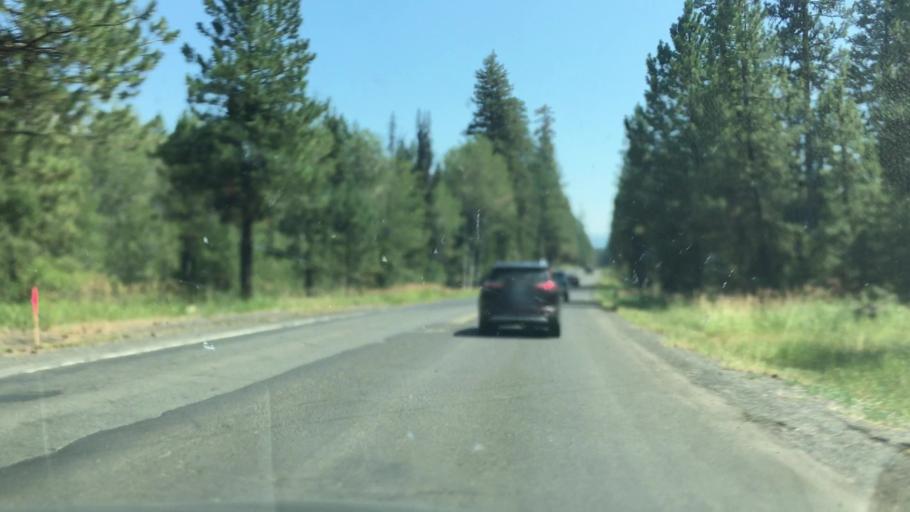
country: US
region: Idaho
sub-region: Valley County
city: McCall
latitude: 44.9248
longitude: -116.1420
